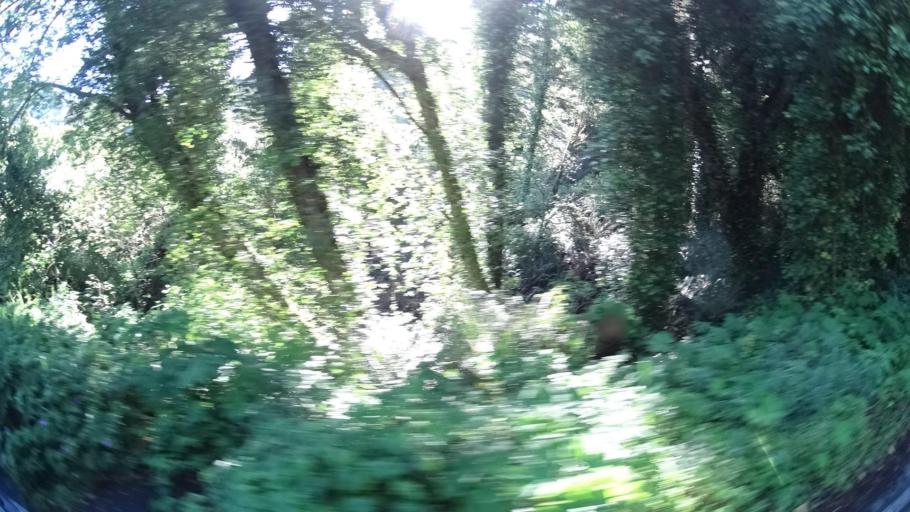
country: US
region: California
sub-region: Humboldt County
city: Westhaven-Moonstone
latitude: 41.1205
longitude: -124.1567
